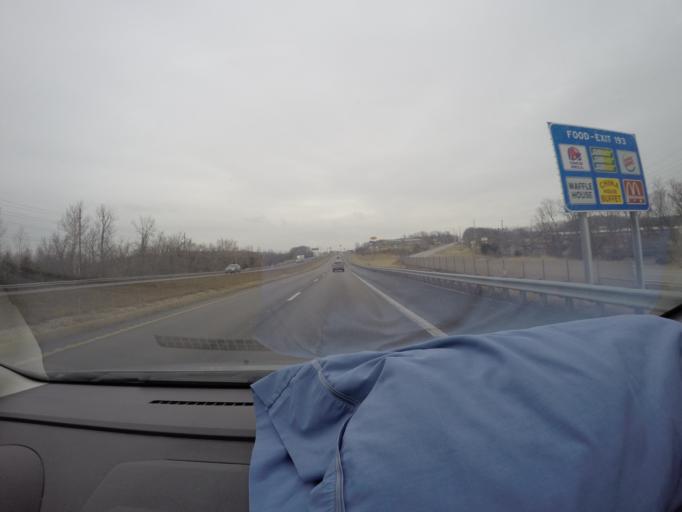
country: US
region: Missouri
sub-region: Warren County
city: Warrenton
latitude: 38.8209
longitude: -91.1527
